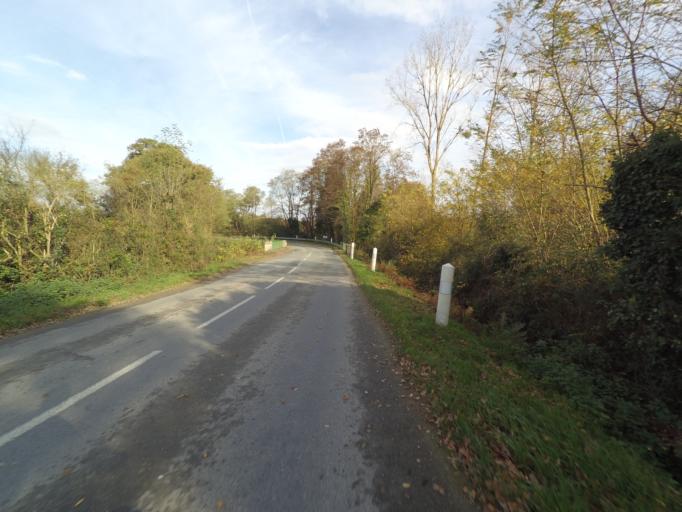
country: FR
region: Pays de la Loire
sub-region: Departement de la Vendee
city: Saint-Hilaire-de-Loulay
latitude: 47.0070
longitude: -1.3658
